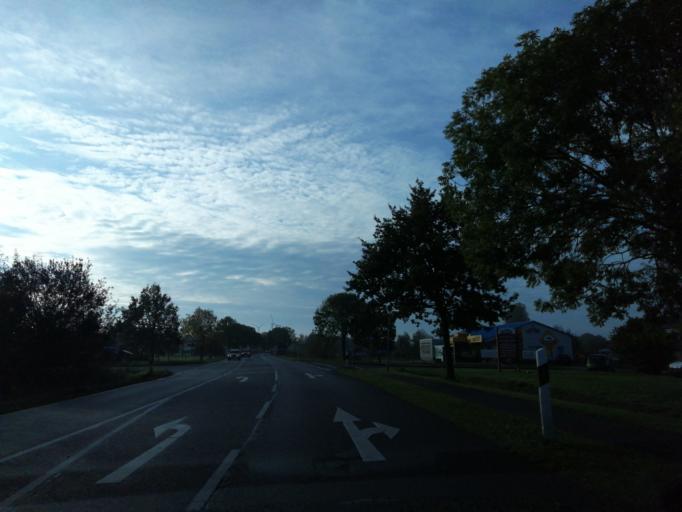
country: DE
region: Lower Saxony
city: Sillenstede
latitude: 53.6318
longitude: 8.0148
